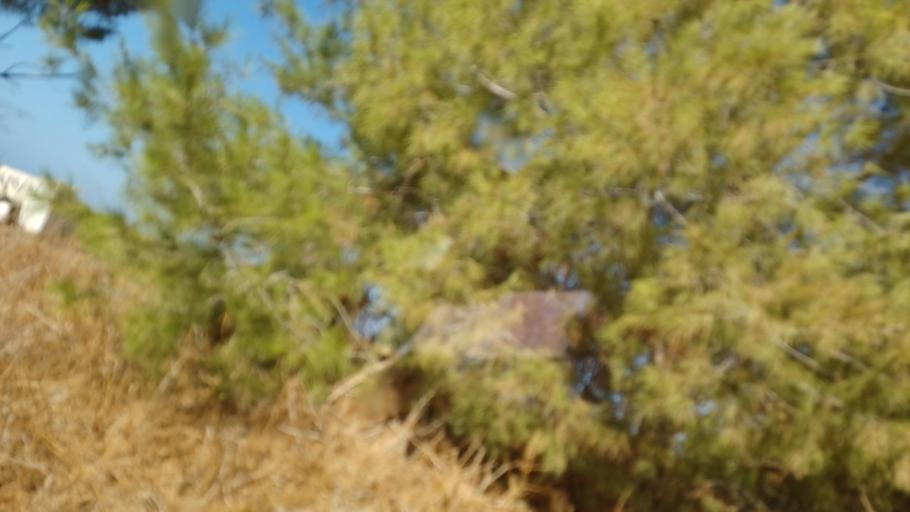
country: CY
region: Pafos
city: Polis
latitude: 35.0433
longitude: 32.4566
